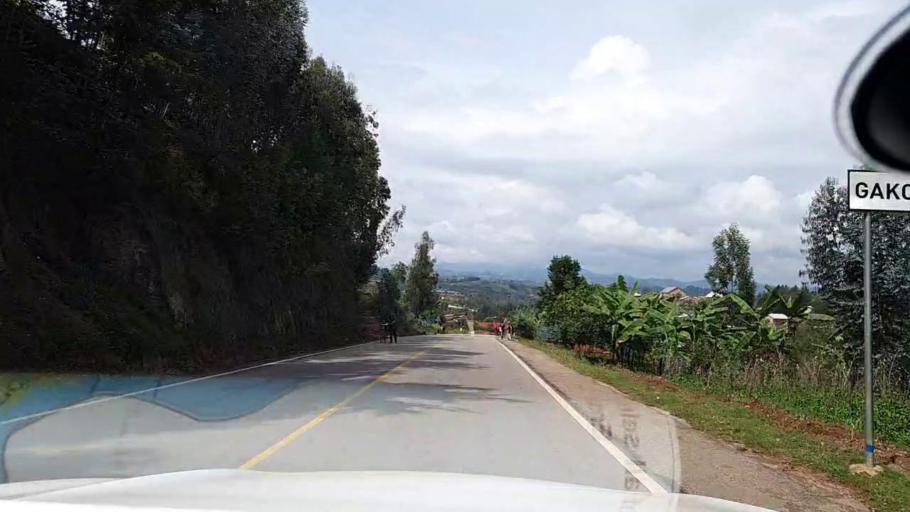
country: RW
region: Southern Province
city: Nzega
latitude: -2.4847
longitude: 29.5187
